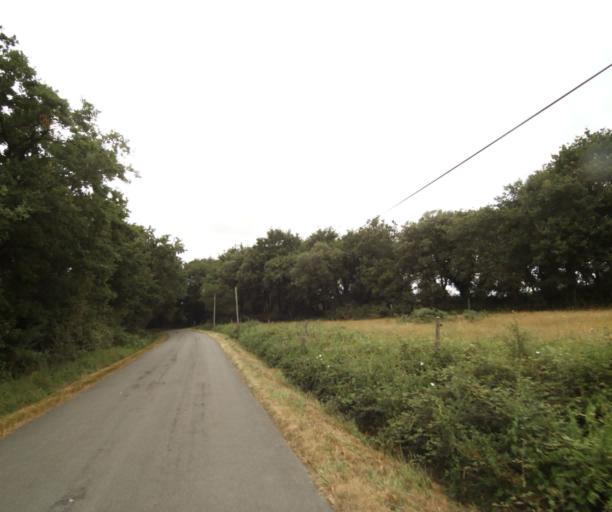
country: FR
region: Pays de la Loire
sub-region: Departement de la Vendee
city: Chateau-d'Olonne
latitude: 46.4882
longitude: -1.6876
